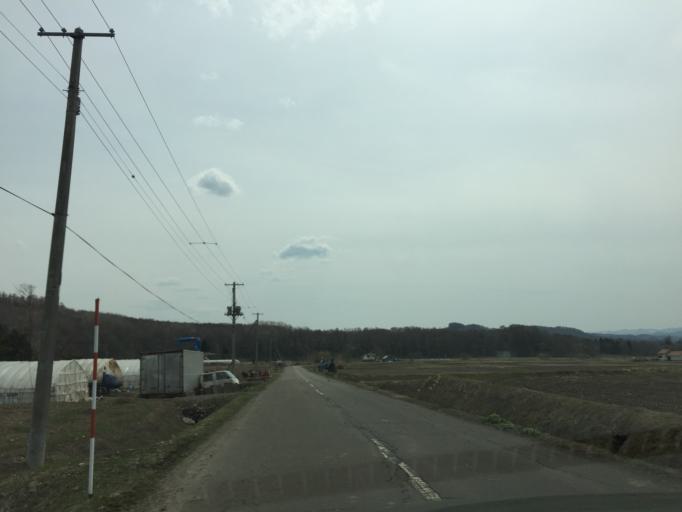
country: JP
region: Hokkaido
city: Ashibetsu
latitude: 43.6179
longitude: 142.2149
